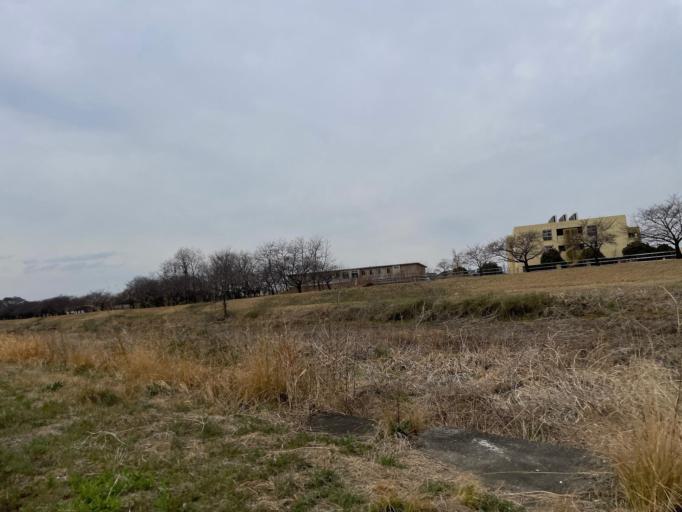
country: JP
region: Saitama
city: Kodamacho-kodamaminami
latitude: 36.1817
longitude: 139.1423
